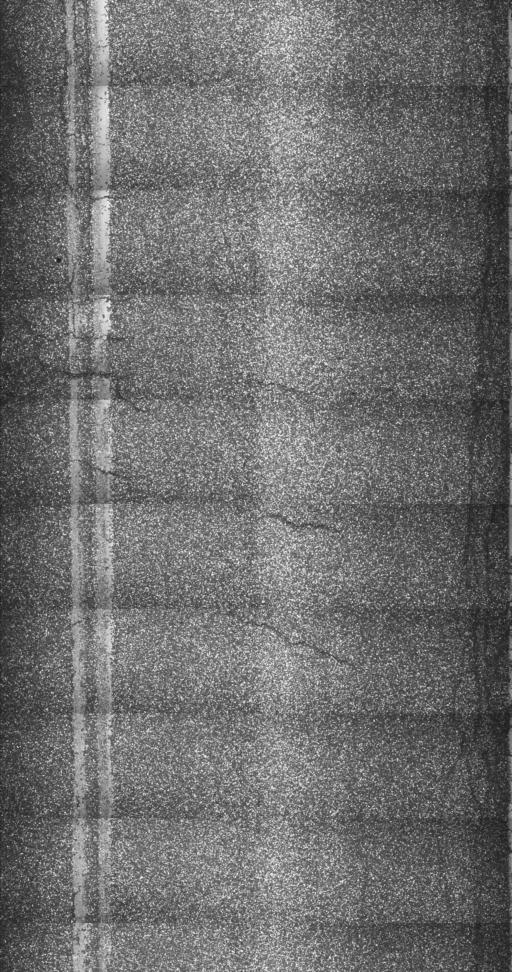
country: US
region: Vermont
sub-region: Caledonia County
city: Hardwick
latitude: 44.4042
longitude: -72.4101
